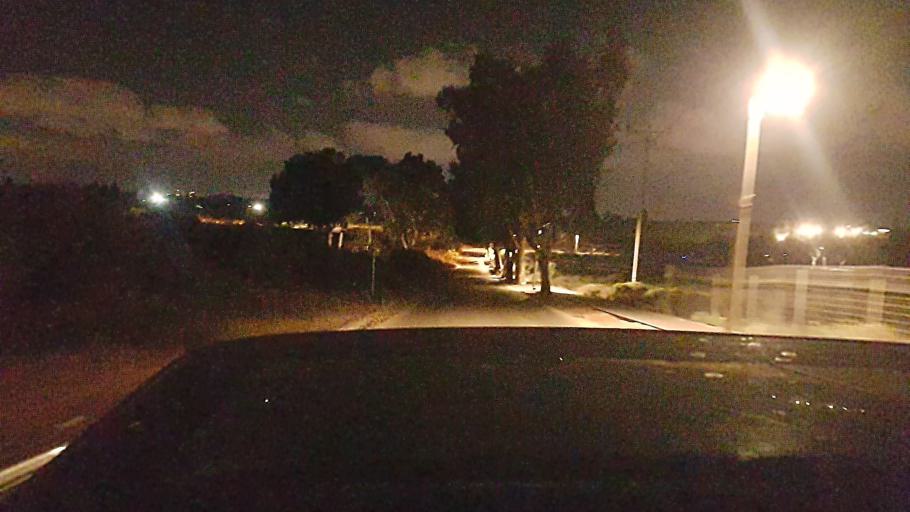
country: IL
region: Central District
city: Hod HaSharon
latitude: 32.1623
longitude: 34.8762
